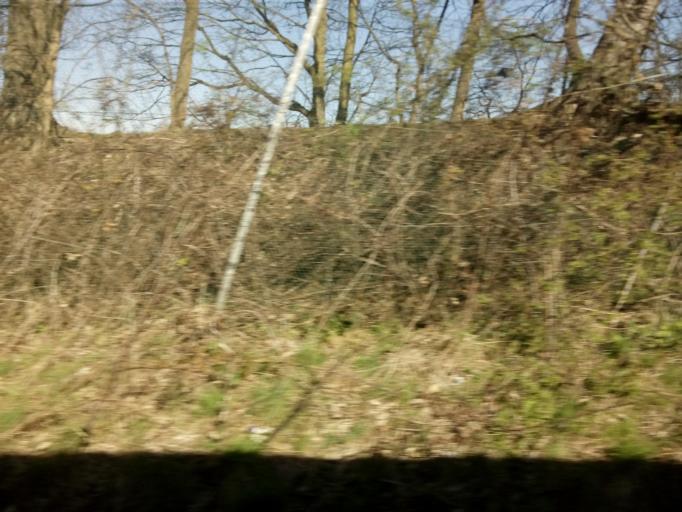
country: GB
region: Scotland
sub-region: Fife
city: Crossgates
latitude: 56.0431
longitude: -3.3607
